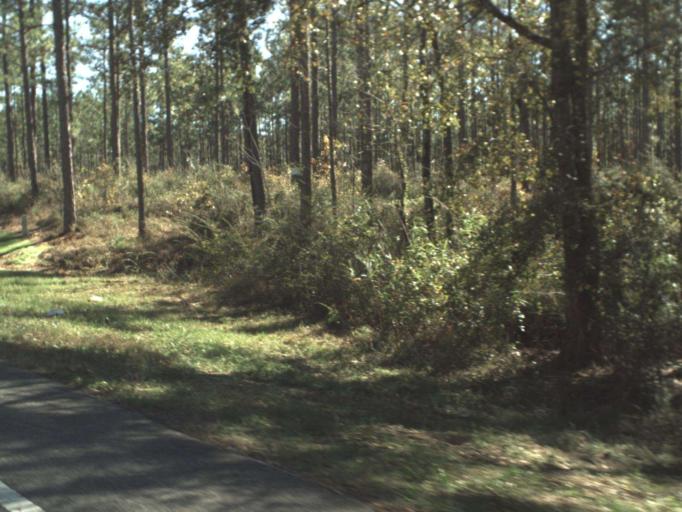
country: US
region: Florida
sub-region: Okaloosa County
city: Crestview
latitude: 30.8500
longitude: -86.7637
